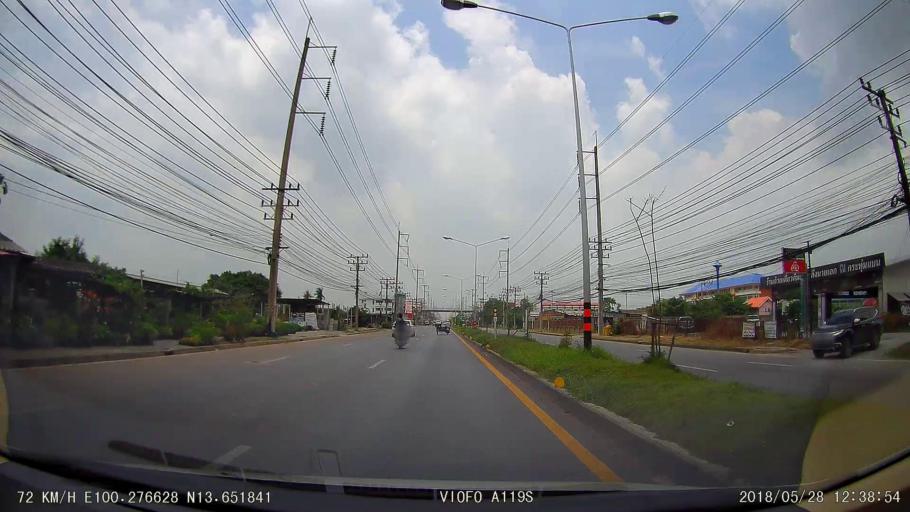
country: TH
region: Samut Sakhon
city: Krathum Baen
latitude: 13.6518
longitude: 100.2768
